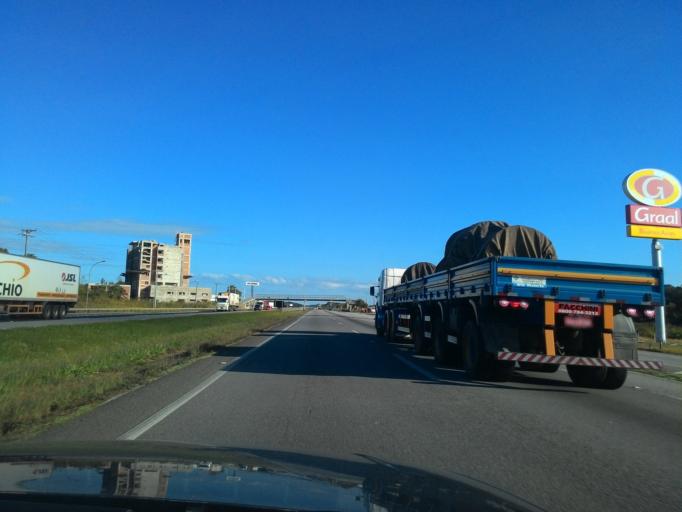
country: BR
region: Sao Paulo
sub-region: Registro
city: Registro
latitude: -24.5268
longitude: -47.8557
